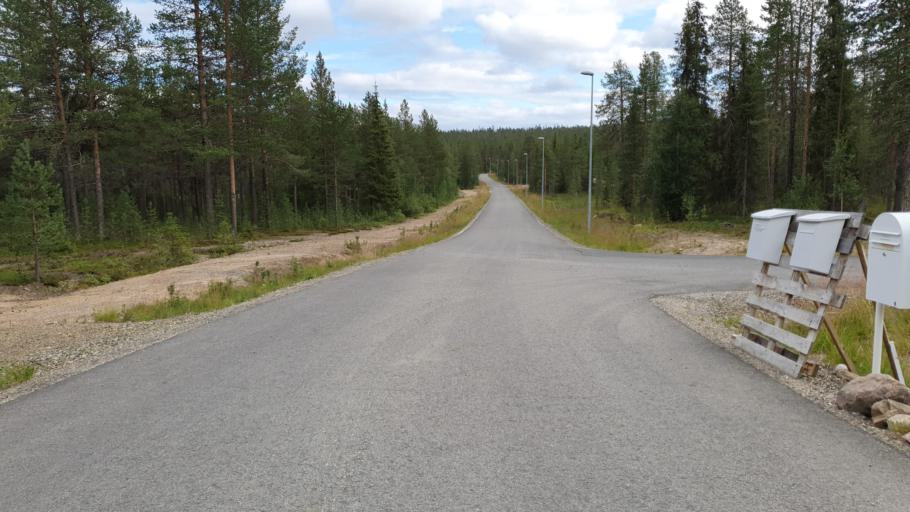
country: FI
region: Lapland
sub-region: Tunturi-Lappi
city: Kolari
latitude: 67.5989
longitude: 24.1373
